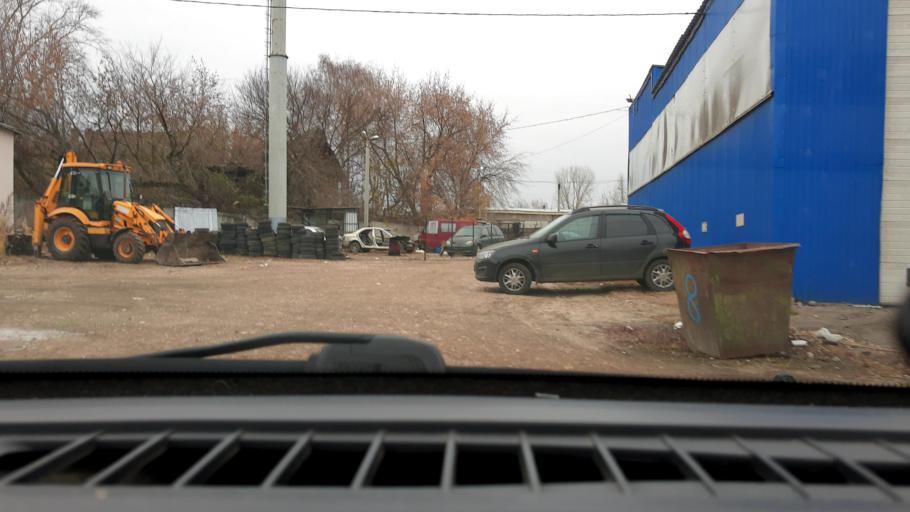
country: RU
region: Nizjnij Novgorod
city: Nizhniy Novgorod
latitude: 56.2843
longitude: 43.9581
